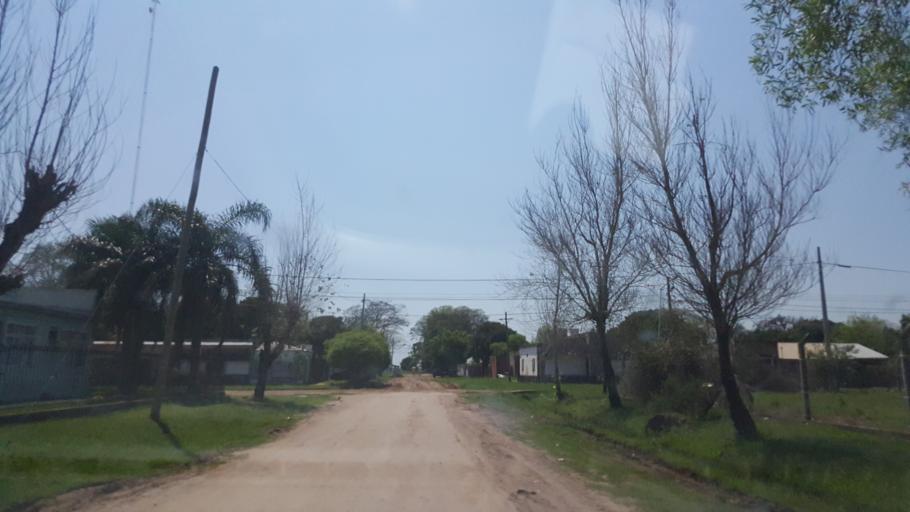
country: AR
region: Corrientes
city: Ita Ibate
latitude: -27.4257
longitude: -57.3398
